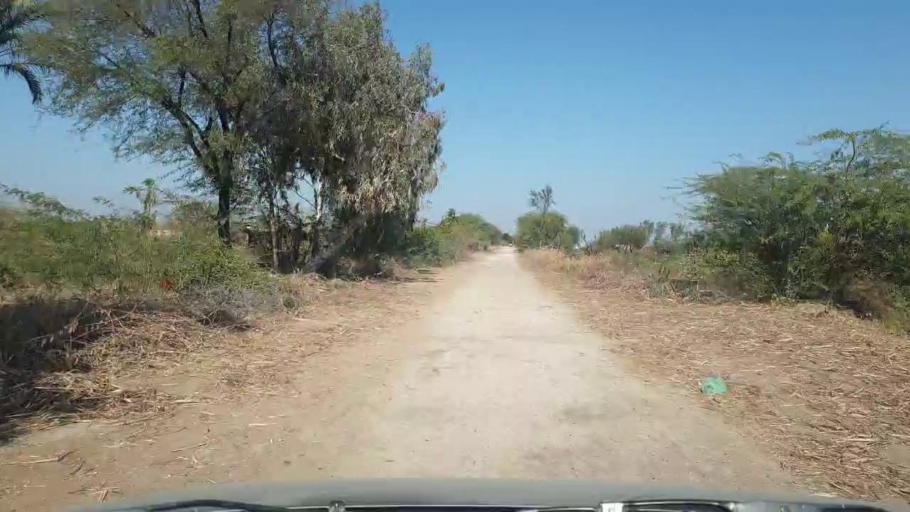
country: PK
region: Sindh
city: Mirwah Gorchani
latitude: 25.3145
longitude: 69.1283
